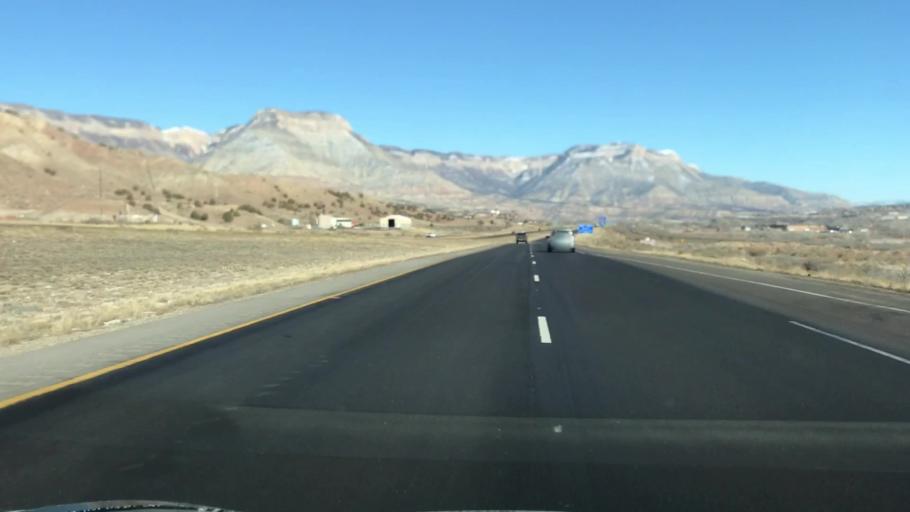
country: US
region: Colorado
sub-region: Garfield County
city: Parachute
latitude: 39.4335
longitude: -108.0706
